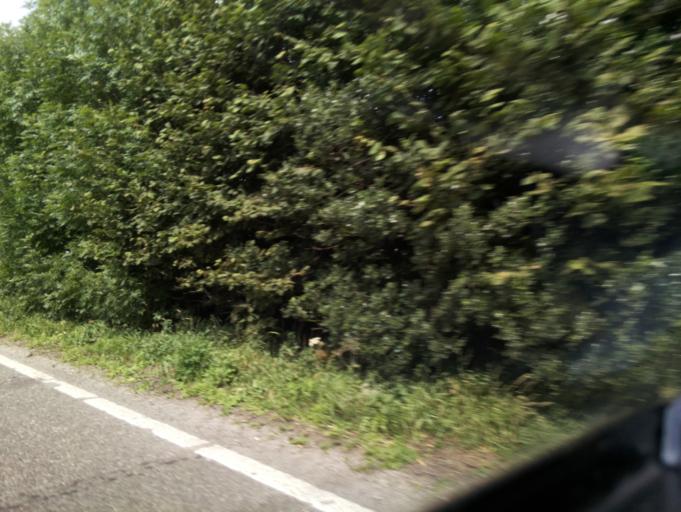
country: GB
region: England
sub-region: Dorset
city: Sherborne
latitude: 50.8150
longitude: -2.5557
